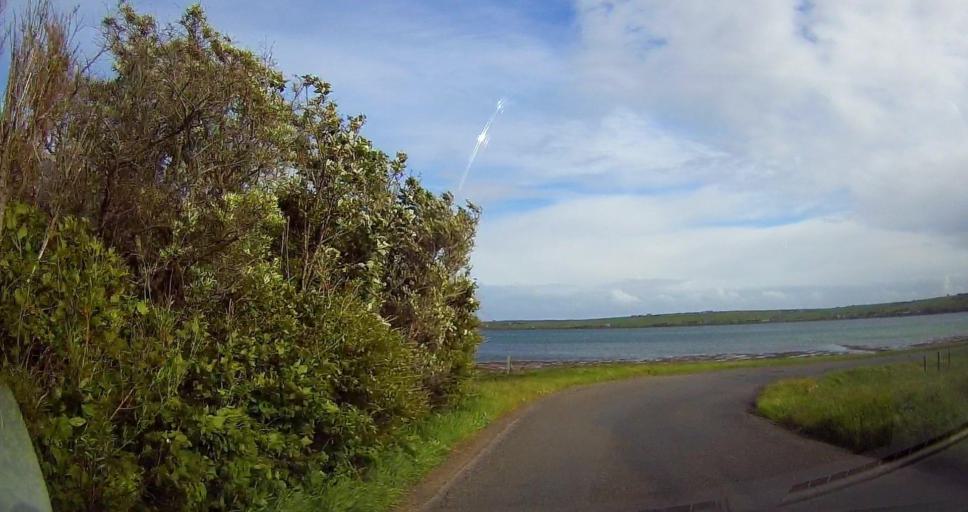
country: GB
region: Scotland
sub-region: Orkney Islands
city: Stromness
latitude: 58.8121
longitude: -3.2000
